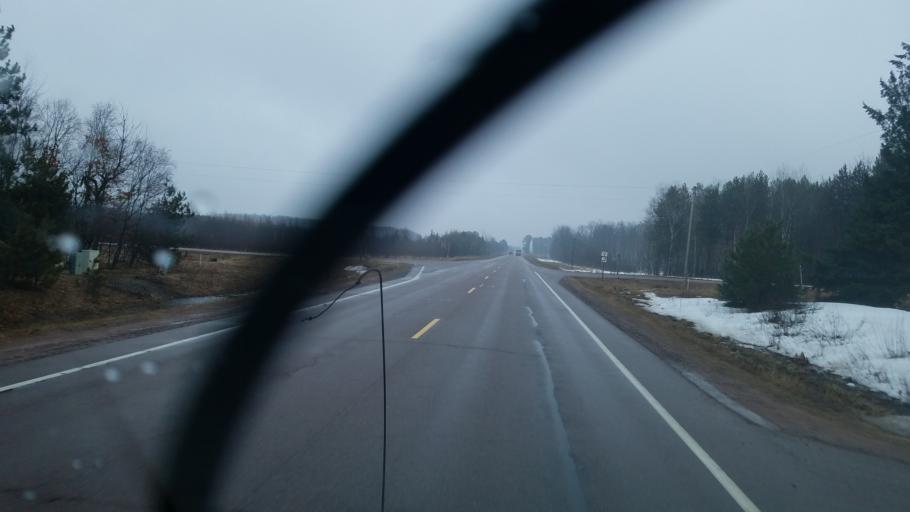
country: US
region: Wisconsin
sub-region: Wood County
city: Marshfield
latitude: 44.4535
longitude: -90.2807
